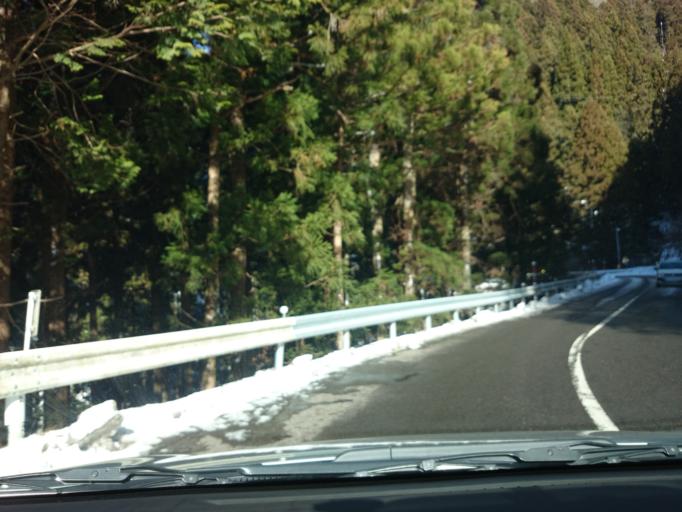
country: JP
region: Gifu
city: Gujo
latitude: 35.7410
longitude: 136.9876
